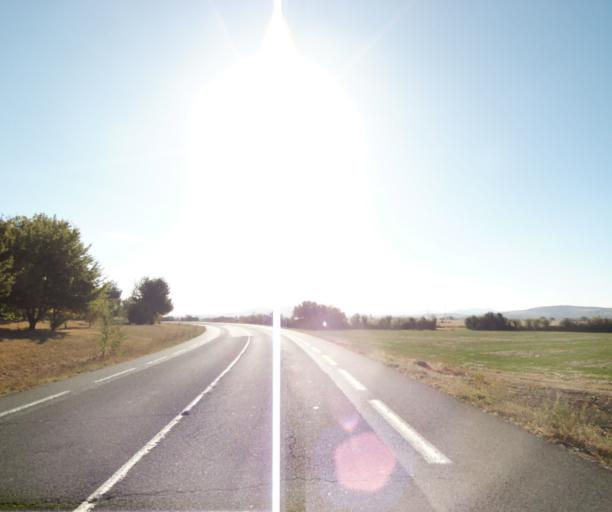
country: FR
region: Auvergne
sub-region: Departement du Puy-de-Dome
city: Malintrat
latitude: 45.8115
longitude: 3.1807
